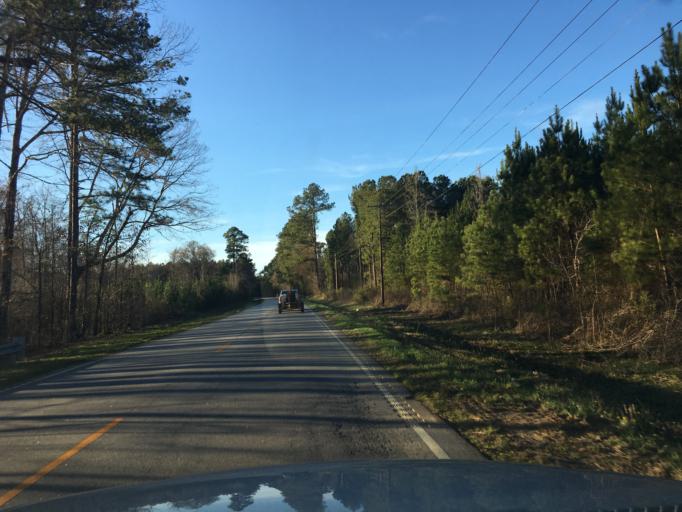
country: US
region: South Carolina
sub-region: Saluda County
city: Saluda
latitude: 34.0378
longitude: -81.8084
